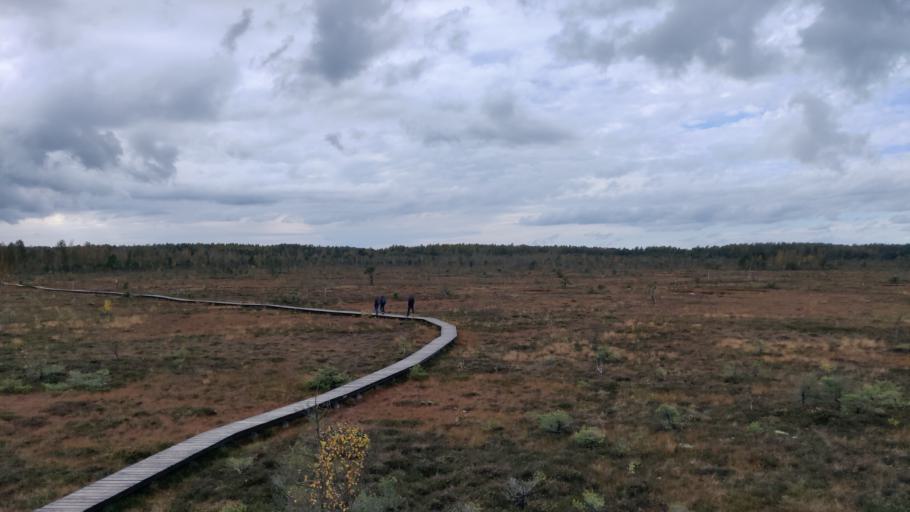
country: LT
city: Rusne
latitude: 55.3958
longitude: 21.3598
